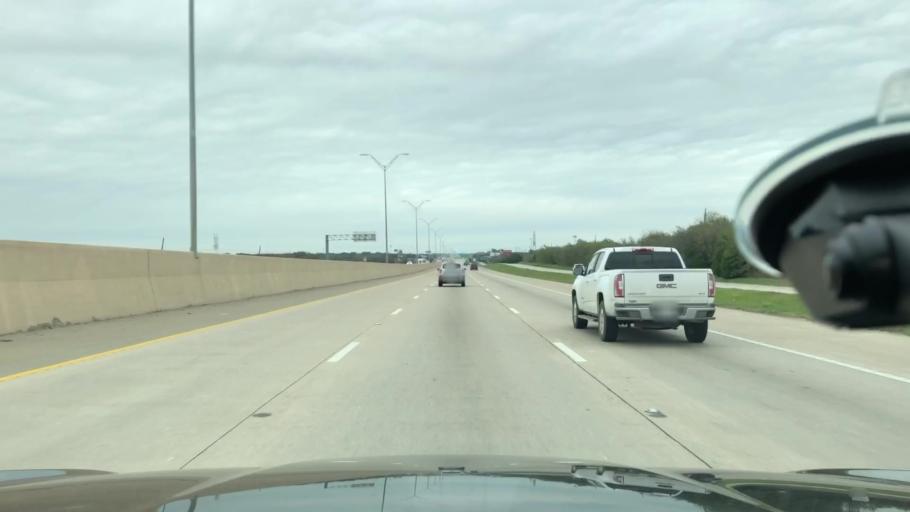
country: US
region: Texas
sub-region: Dallas County
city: Glenn Heights
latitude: 32.5504
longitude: -96.8223
